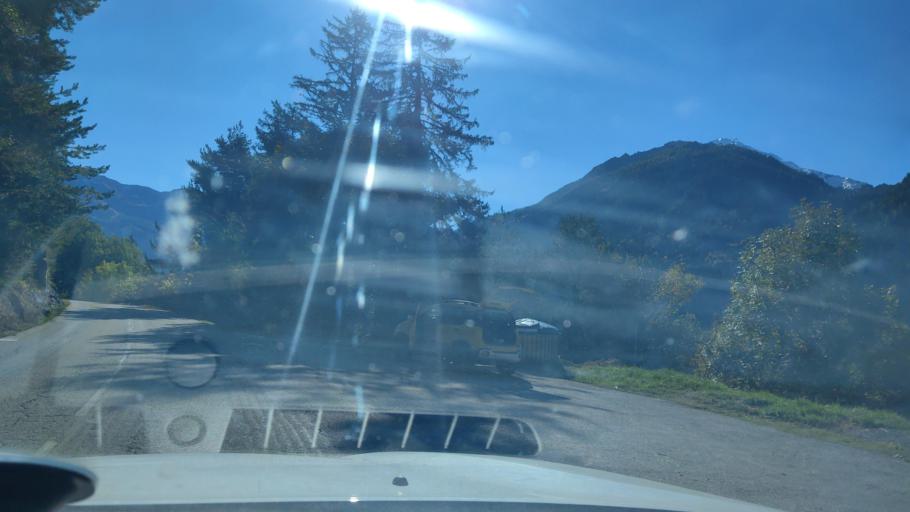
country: FR
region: Rhone-Alpes
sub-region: Departement de la Savoie
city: Seez
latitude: 45.6166
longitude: 6.8321
